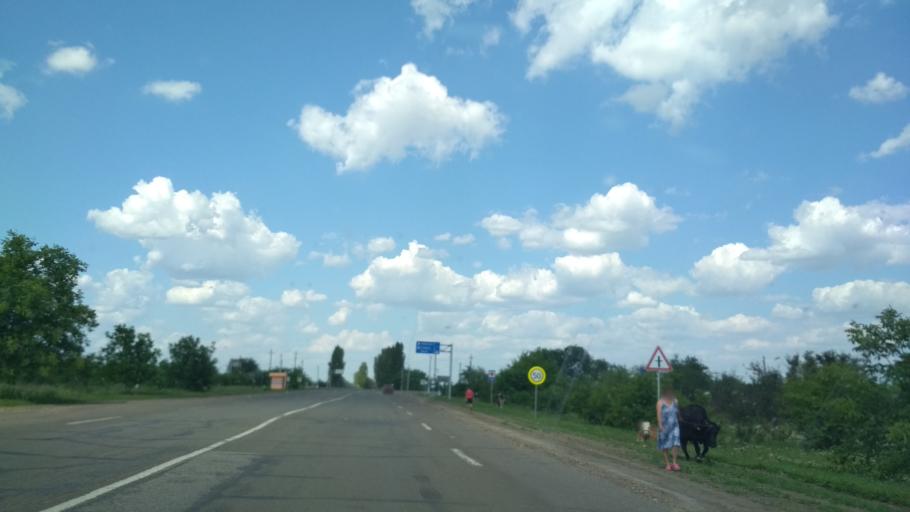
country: MD
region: Chisinau
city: Vadul lui Voda
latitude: 47.1177
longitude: 29.1090
